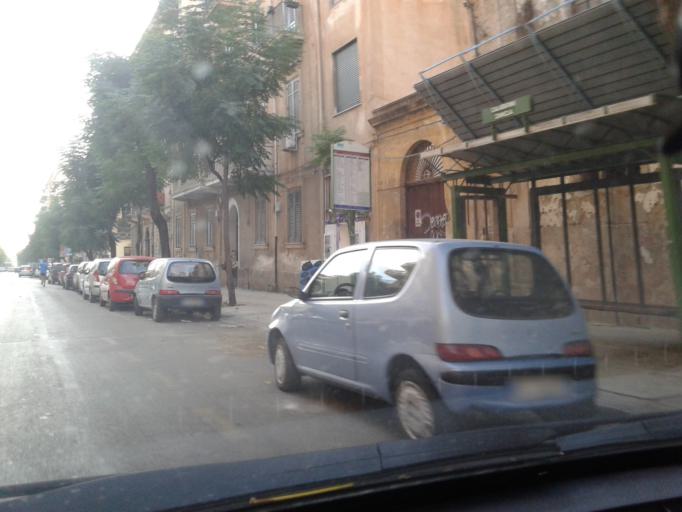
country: IT
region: Sicily
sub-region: Palermo
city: Palermo
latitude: 38.1062
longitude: 13.3379
